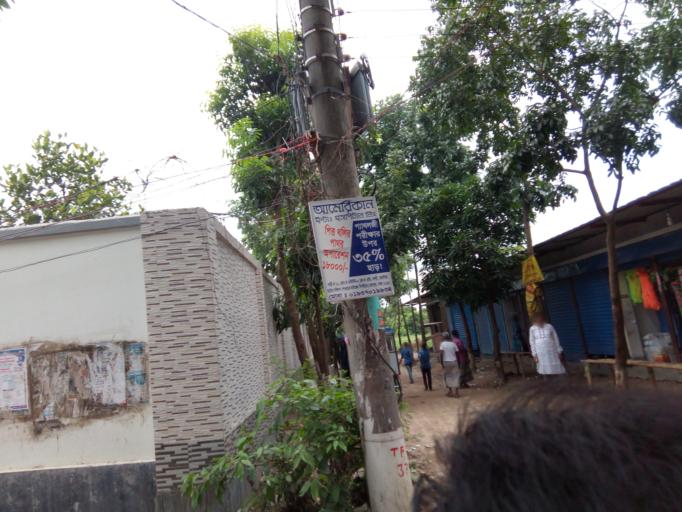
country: BD
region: Dhaka
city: Paltan
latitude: 23.7601
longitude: 90.4757
